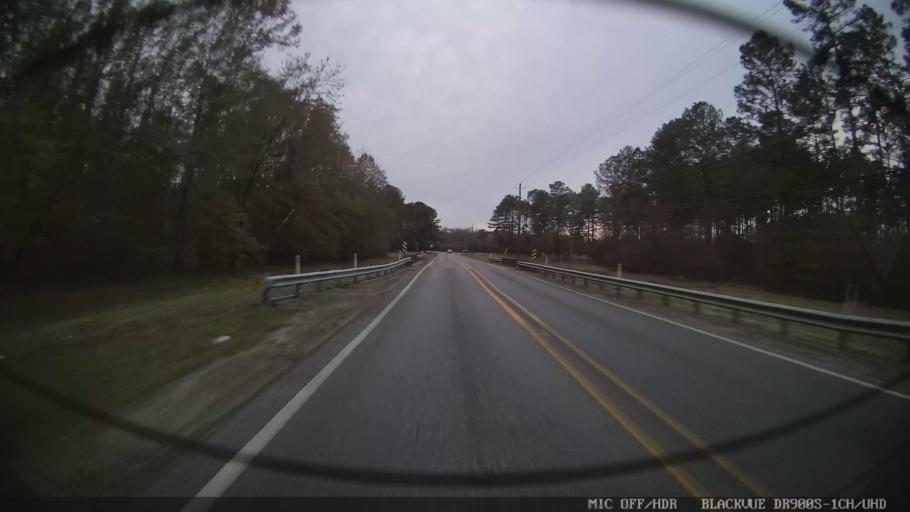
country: US
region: Mississippi
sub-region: Clarke County
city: Quitman
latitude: 32.0429
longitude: -88.7506
